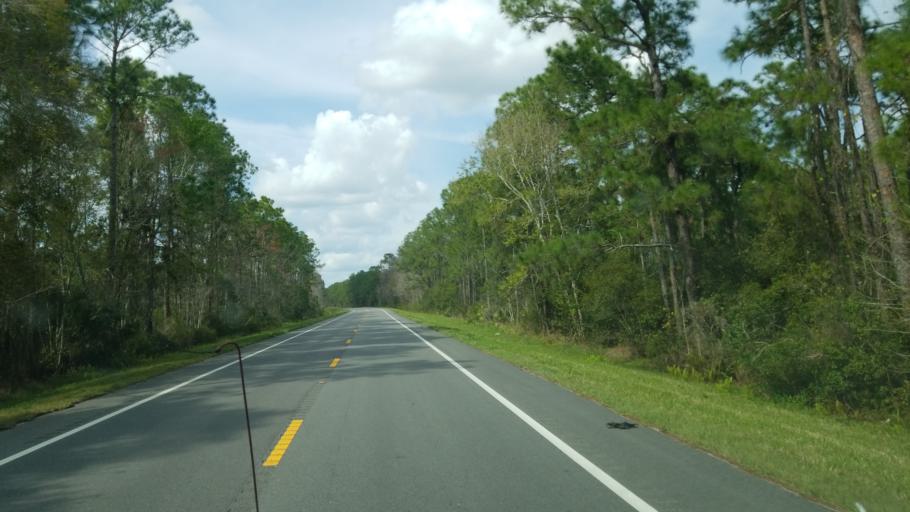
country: US
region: Florida
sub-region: Indian River County
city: Fellsmere
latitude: 27.7905
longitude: -80.9317
